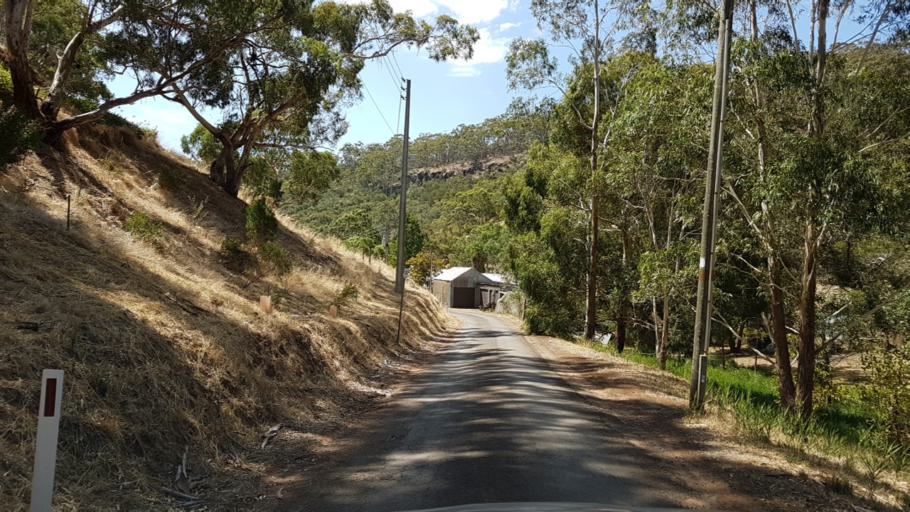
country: AU
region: South Australia
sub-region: Burnside
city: Mount Osmond
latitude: -34.9930
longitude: 138.6543
